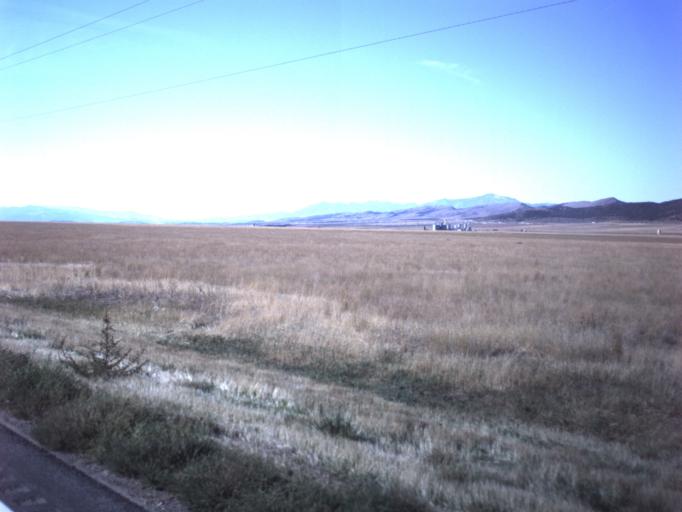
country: US
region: Utah
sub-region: Juab County
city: Nephi
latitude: 39.6360
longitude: -111.8616
